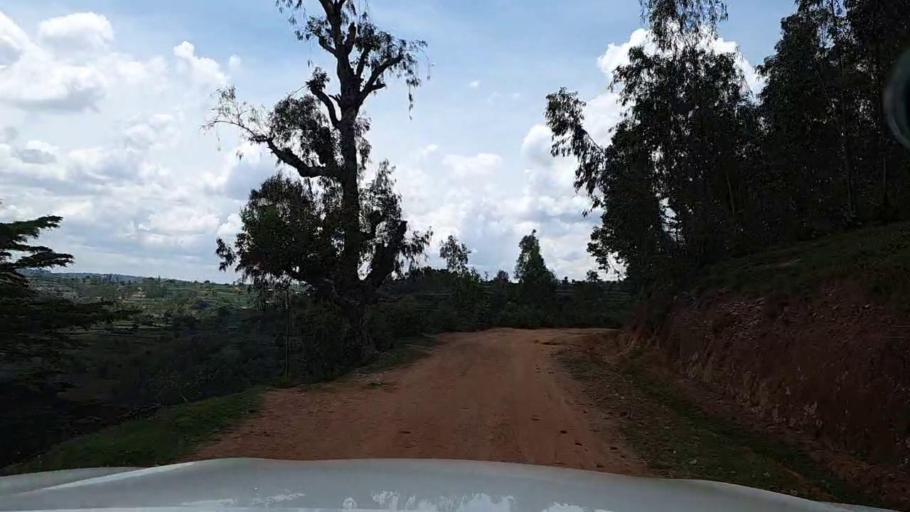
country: RW
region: Southern Province
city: Butare
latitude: -2.7554
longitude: 29.7527
